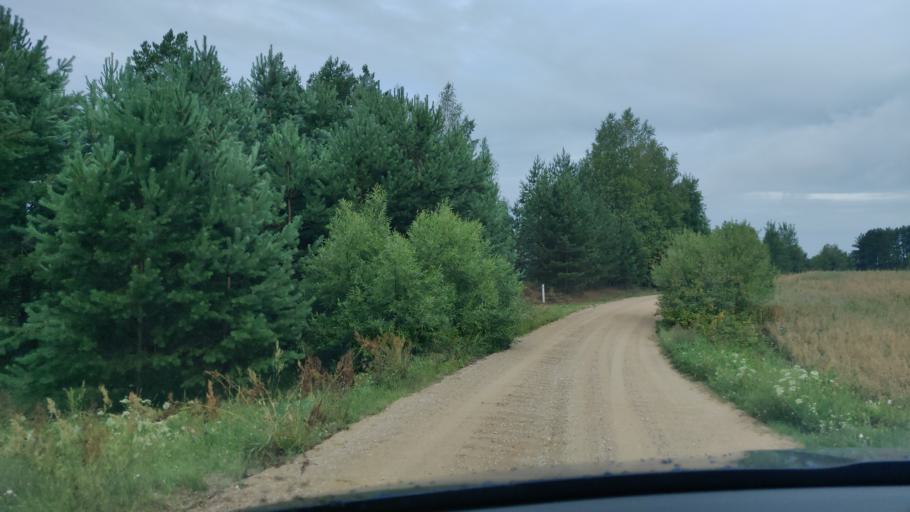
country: LT
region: Vilnius County
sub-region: Trakai
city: Rudiskes
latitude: 54.6102
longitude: 24.8393
